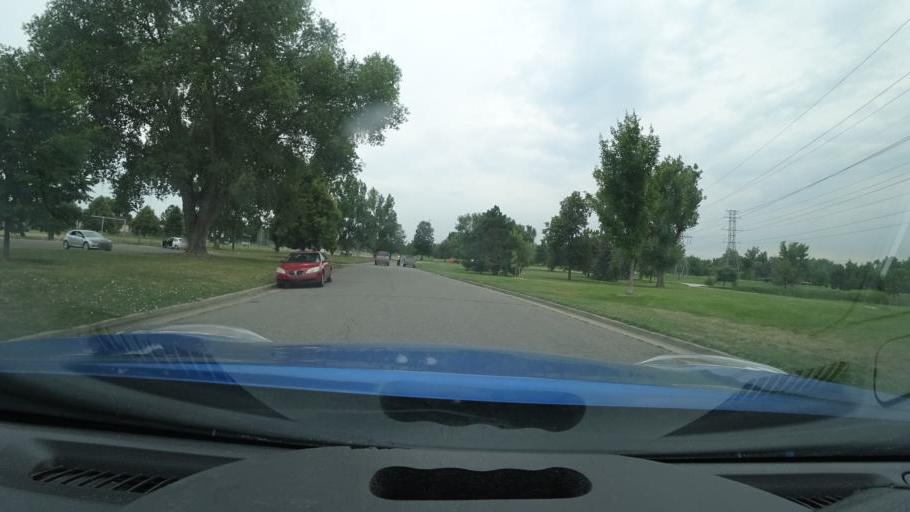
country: US
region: Colorado
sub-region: Arapahoe County
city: Glendale
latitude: 39.6960
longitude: -104.9174
